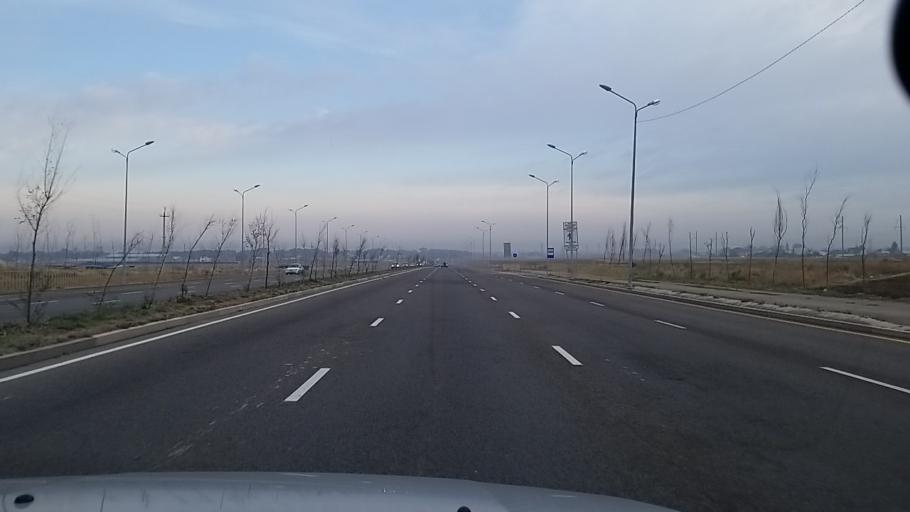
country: KZ
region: Almaty Oblysy
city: Burunday
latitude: 43.3411
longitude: 76.8337
